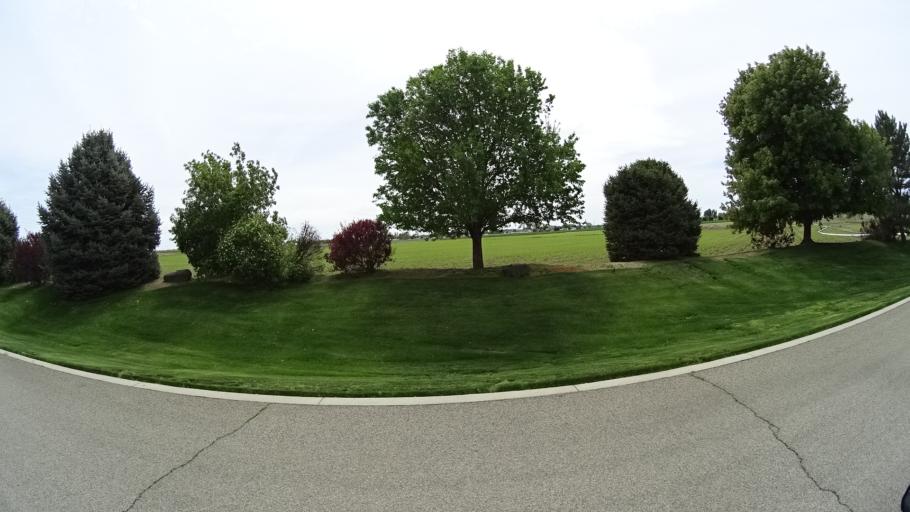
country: US
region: Idaho
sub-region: Ada County
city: Kuna
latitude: 43.5388
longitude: -116.3986
